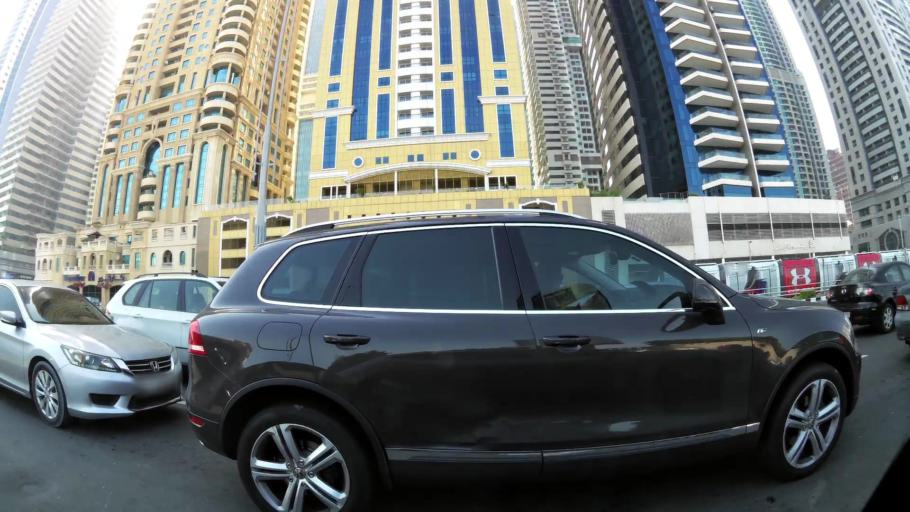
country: AE
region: Dubai
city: Dubai
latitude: 25.0904
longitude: 55.1472
